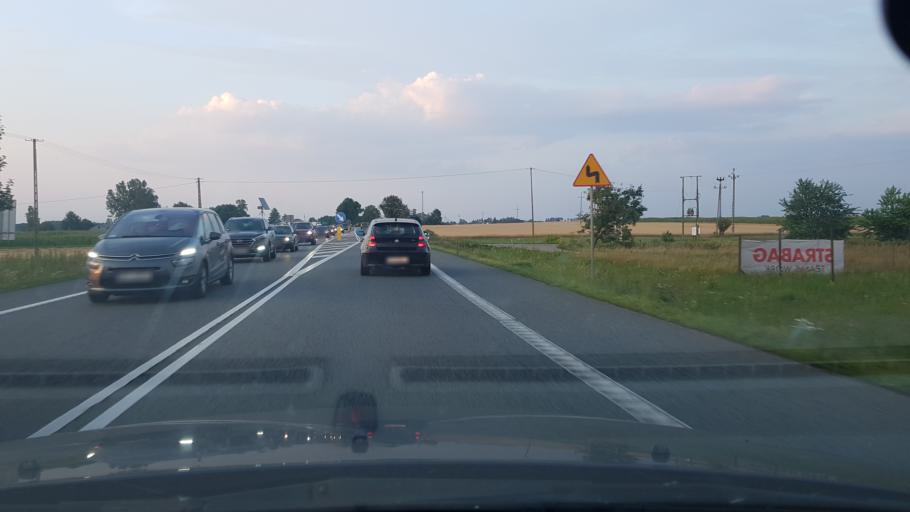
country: PL
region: Masovian Voivodeship
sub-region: Powiat mlawski
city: Wieczfnia Koscielna
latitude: 53.1753
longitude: 20.4257
